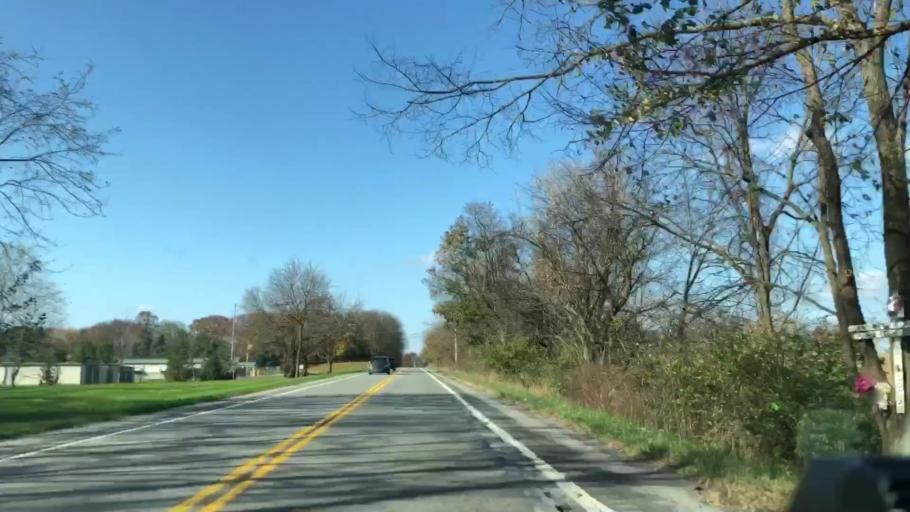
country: US
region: Pennsylvania
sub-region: Montgomery County
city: Sanatoga
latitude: 40.2174
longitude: -75.6069
